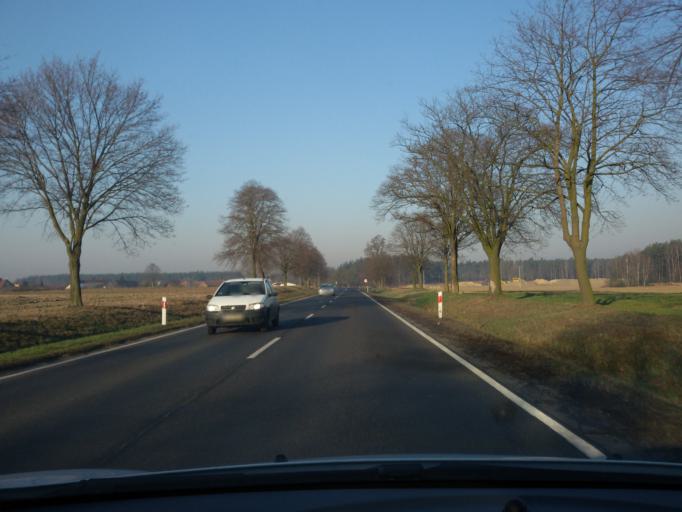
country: PL
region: Greater Poland Voivodeship
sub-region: Powiat leszczynski
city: Swieciechowa
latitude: 51.8233
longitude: 16.4161
